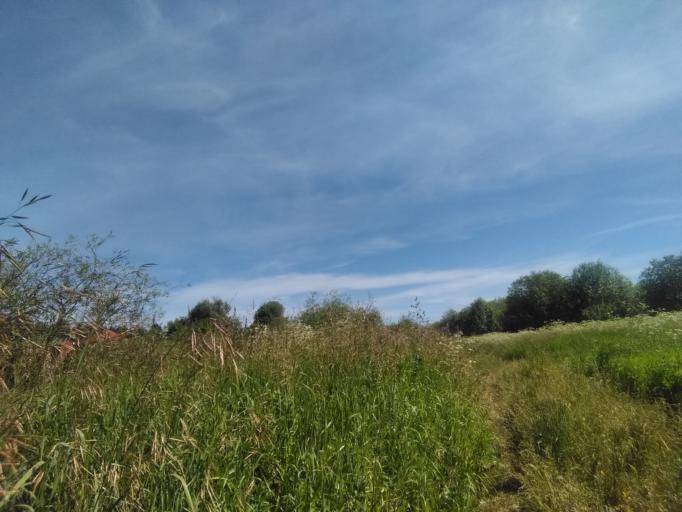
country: RU
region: Udmurtiya
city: Khokhryaki
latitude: 56.8547
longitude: 53.4087
